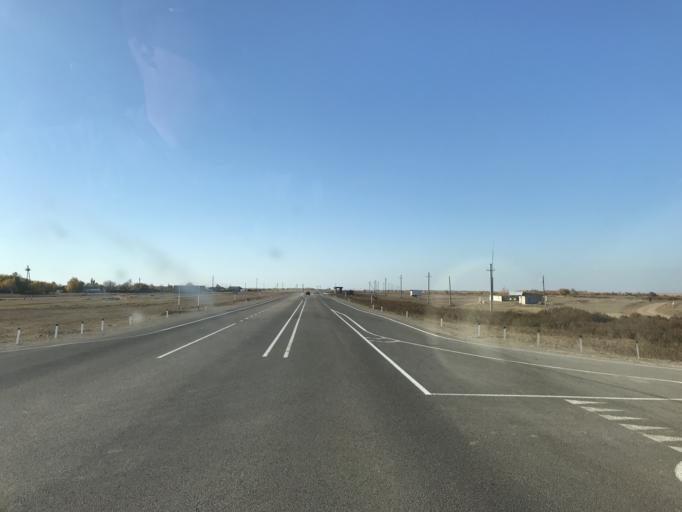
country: KZ
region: Pavlodar
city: Koktobe
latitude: 51.5042
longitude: 77.6981
